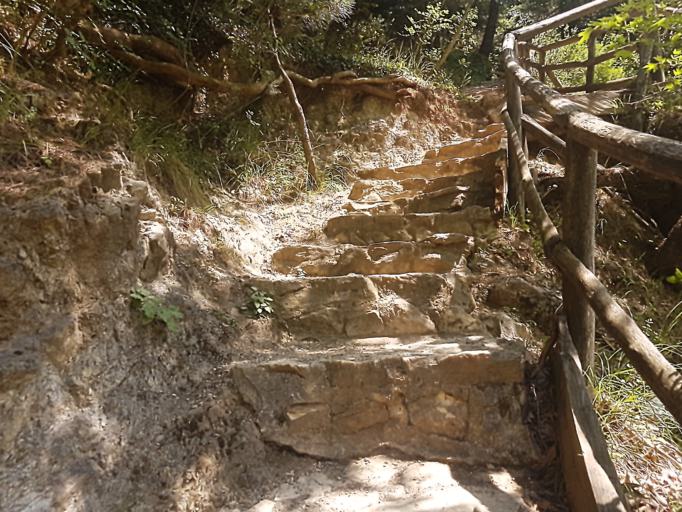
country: GR
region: Central Greece
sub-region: Nomos Evvoias
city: Roviai
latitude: 38.8721
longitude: 23.2933
